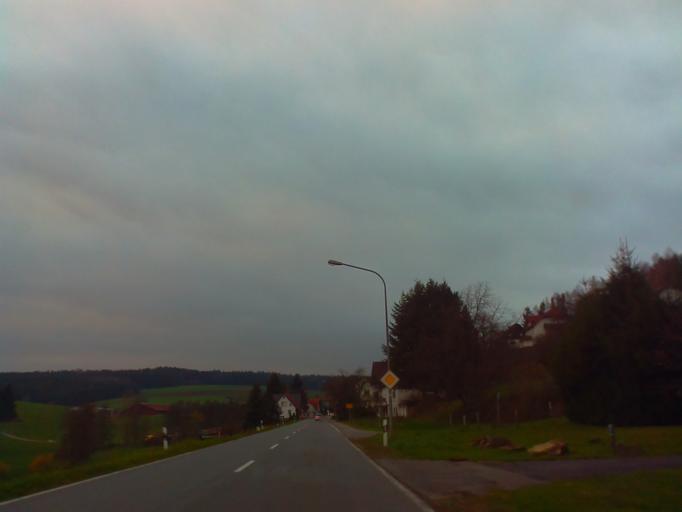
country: DE
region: Hesse
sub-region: Regierungsbezirk Darmstadt
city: Beerfelden
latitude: 49.5857
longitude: 8.9321
